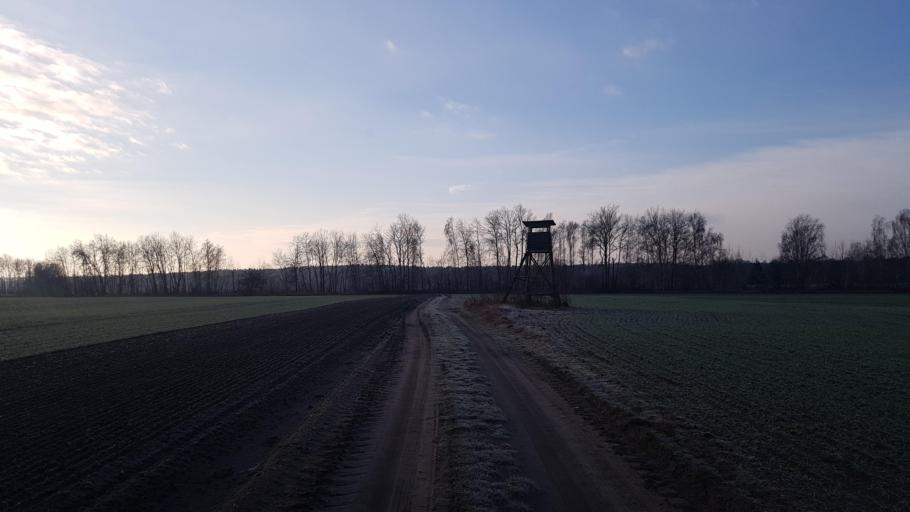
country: DE
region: Brandenburg
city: Ruckersdorf
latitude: 51.5359
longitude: 13.6031
